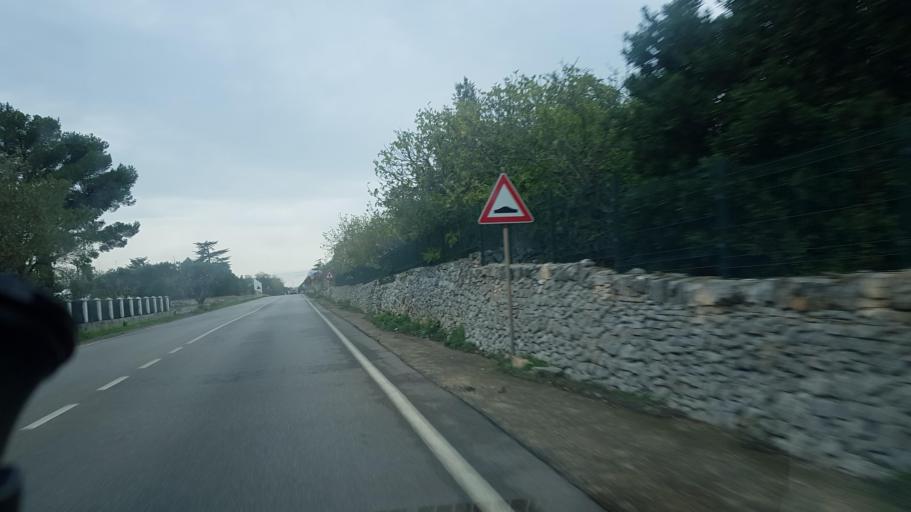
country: IT
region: Apulia
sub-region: Provincia di Brindisi
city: Ostuni
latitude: 40.7196
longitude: 17.6095
